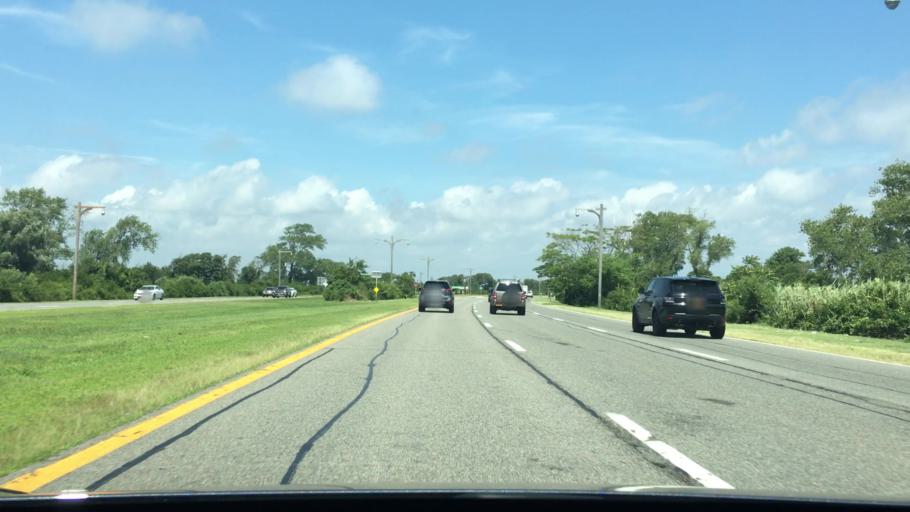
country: US
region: New York
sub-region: Nassau County
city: Point Lookout
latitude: 40.6189
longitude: -73.5587
